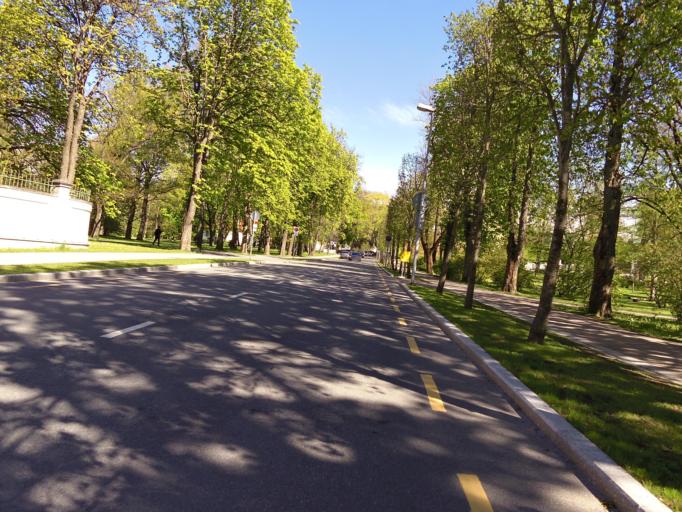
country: EE
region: Harju
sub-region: Tallinna linn
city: Tallinn
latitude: 59.4374
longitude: 24.7933
